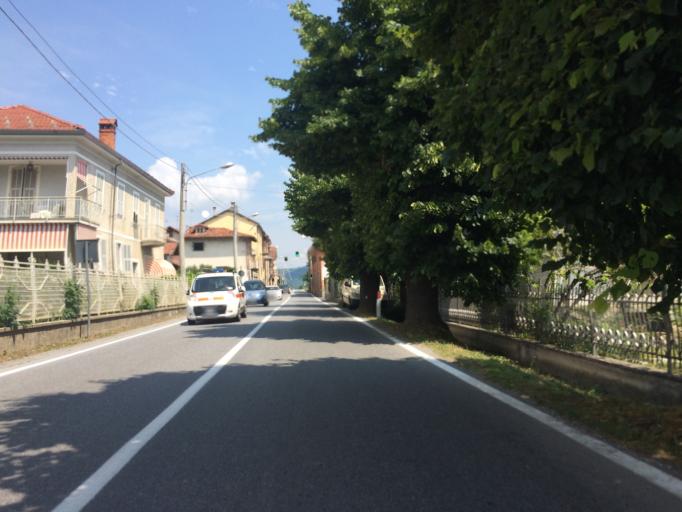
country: IT
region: Piedmont
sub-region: Provincia di Cuneo
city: Bagnasco
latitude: 44.3063
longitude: 8.0459
